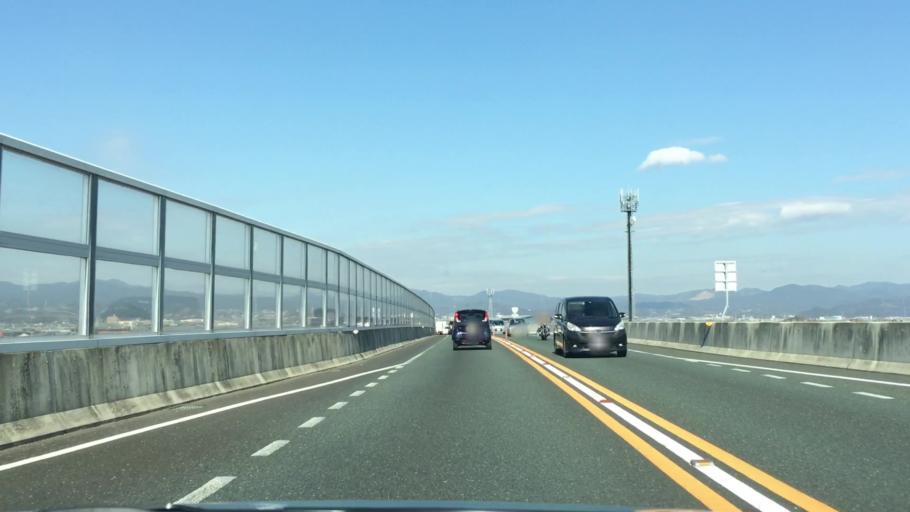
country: JP
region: Aichi
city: Kozakai-cho
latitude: 34.7857
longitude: 137.3326
